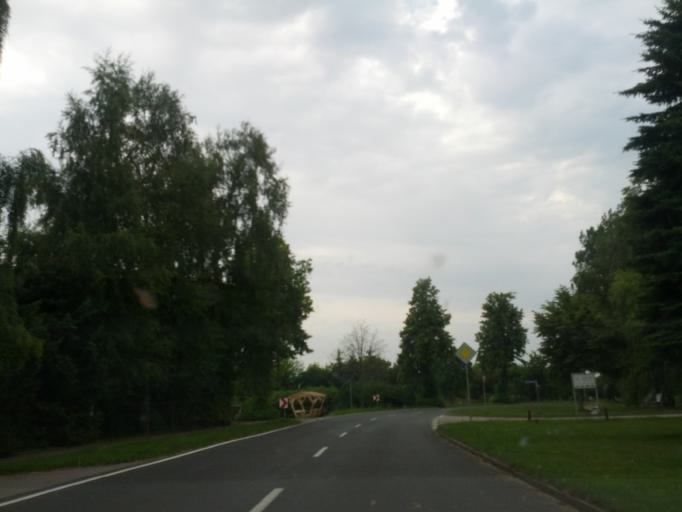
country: DE
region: Mecklenburg-Vorpommern
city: Kropelin
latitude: 54.0262
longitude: 11.7911
